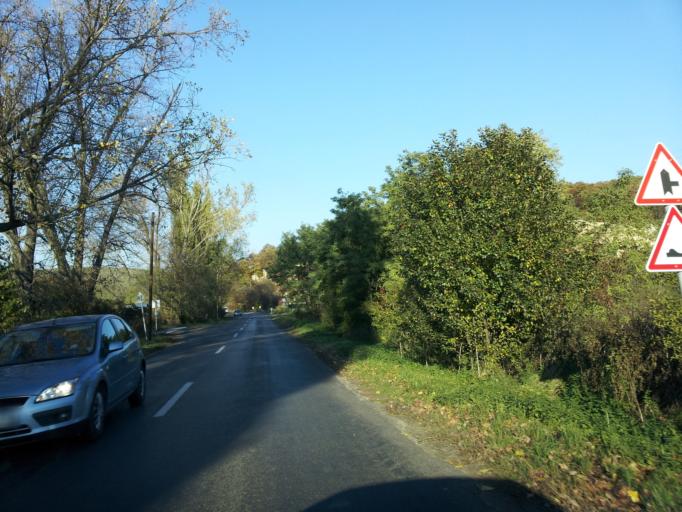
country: HU
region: Fejer
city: Bodajk
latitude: 47.3153
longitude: 18.2052
